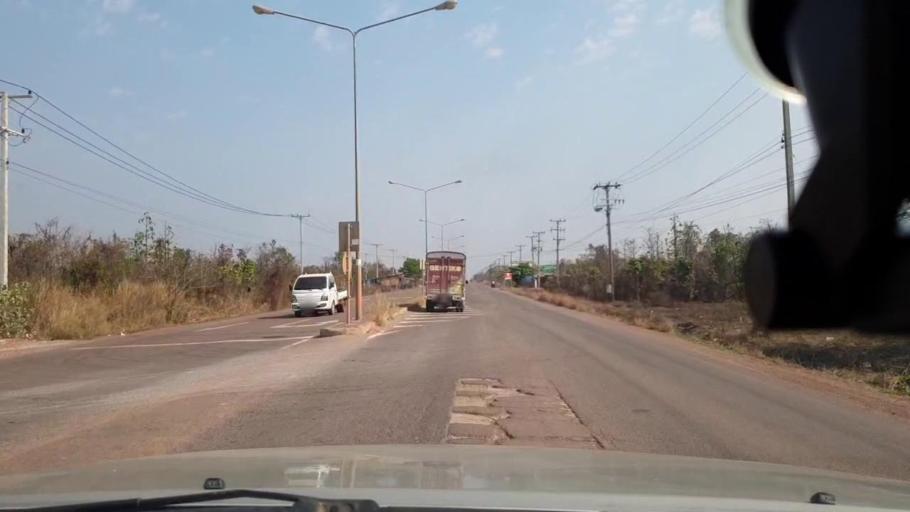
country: LA
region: Vientiane
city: Vientiane
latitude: 18.0152
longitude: 102.7238
